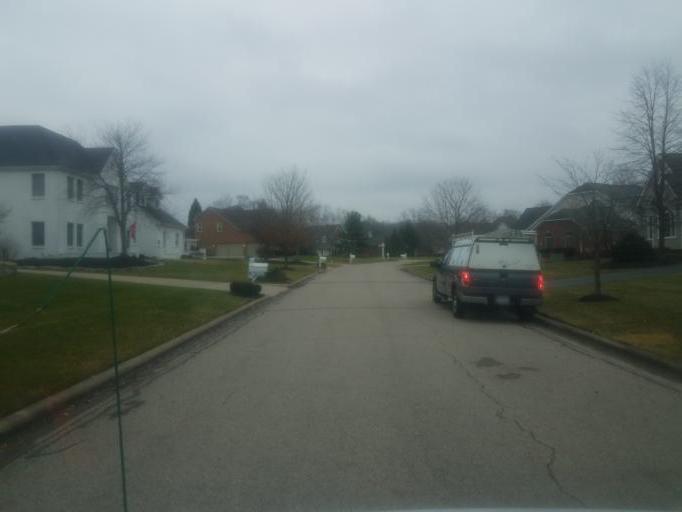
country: US
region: Ohio
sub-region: Franklin County
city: Westerville
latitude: 40.1706
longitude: -82.9495
